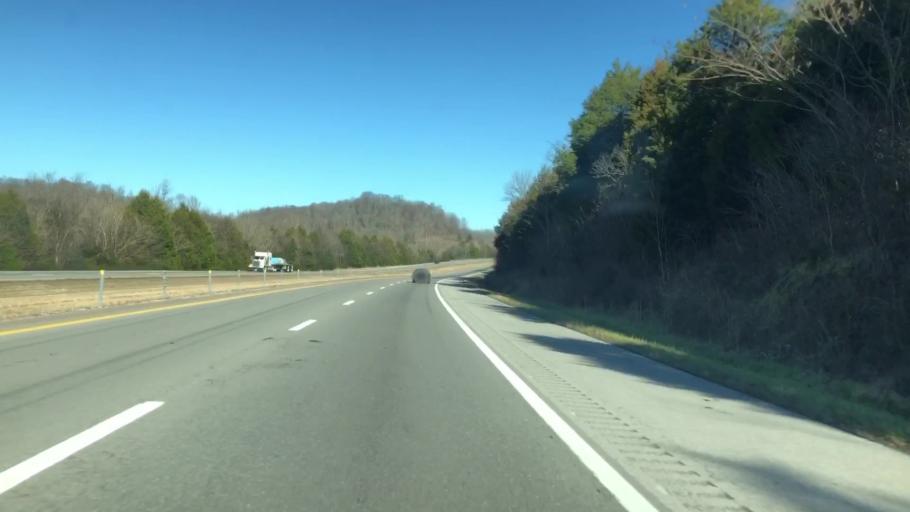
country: US
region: Tennessee
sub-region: Marshall County
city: Cornersville
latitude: 35.2395
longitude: -86.8878
